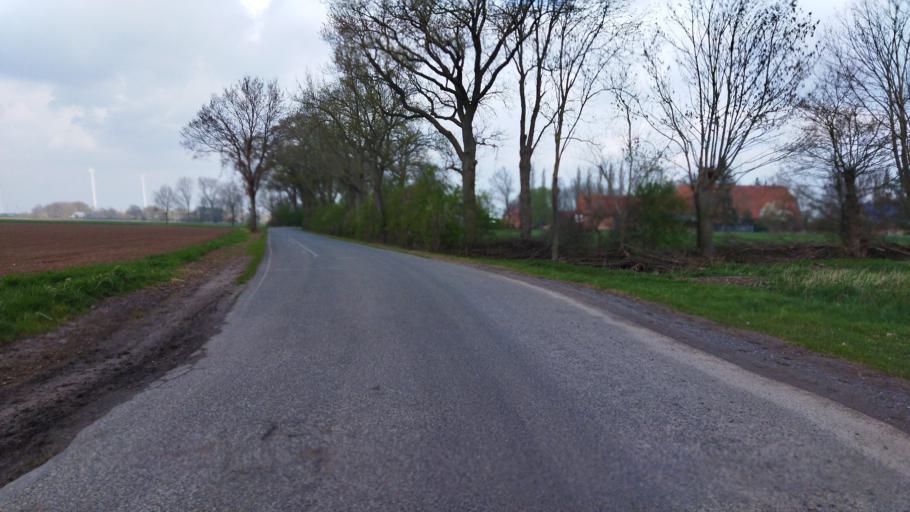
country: DE
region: Lower Saxony
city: Hilgermissen
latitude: 52.8369
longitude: 9.1894
